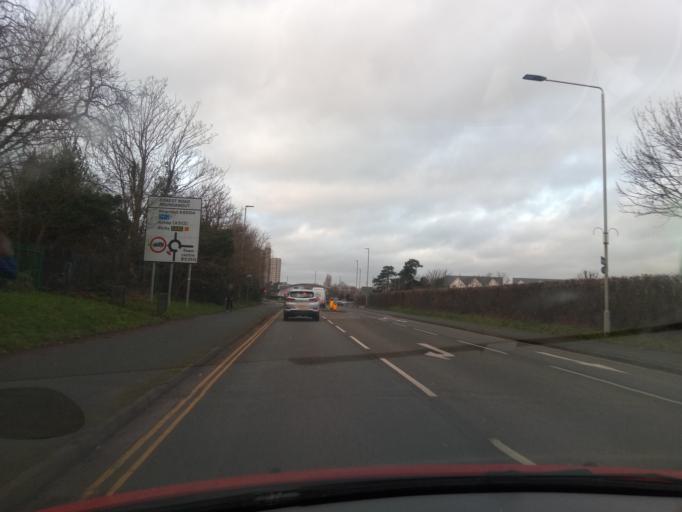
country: GB
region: England
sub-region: Leicestershire
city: Loughborough
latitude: 52.7634
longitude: -1.2159
